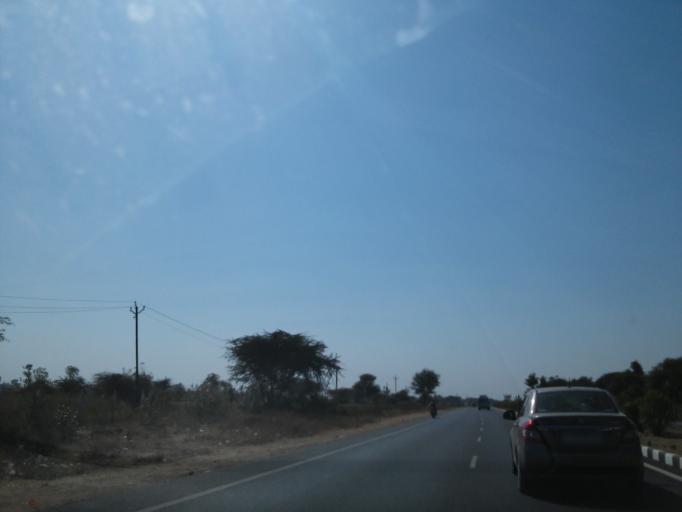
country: IN
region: Gujarat
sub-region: Sabar Kantha
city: Himatnagar
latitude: 23.4753
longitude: 72.8814
